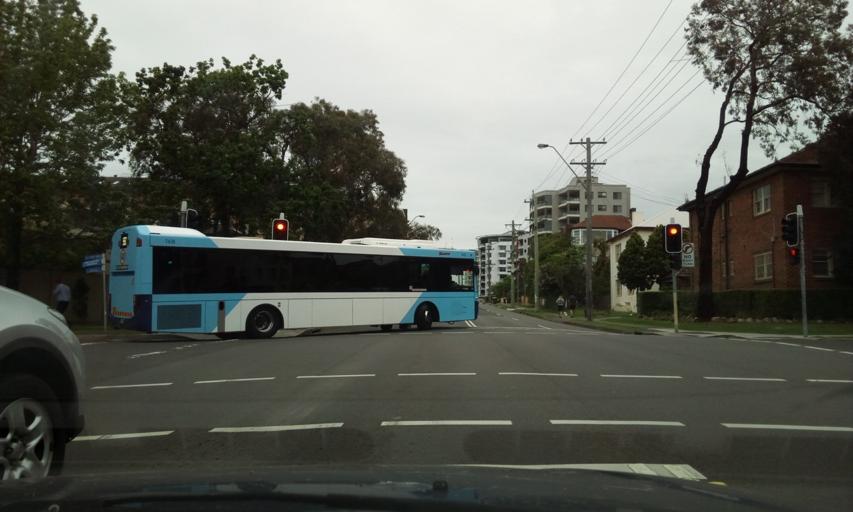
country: AU
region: New South Wales
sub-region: Wollongong
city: Wollongong
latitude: -34.4223
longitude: 150.9006
